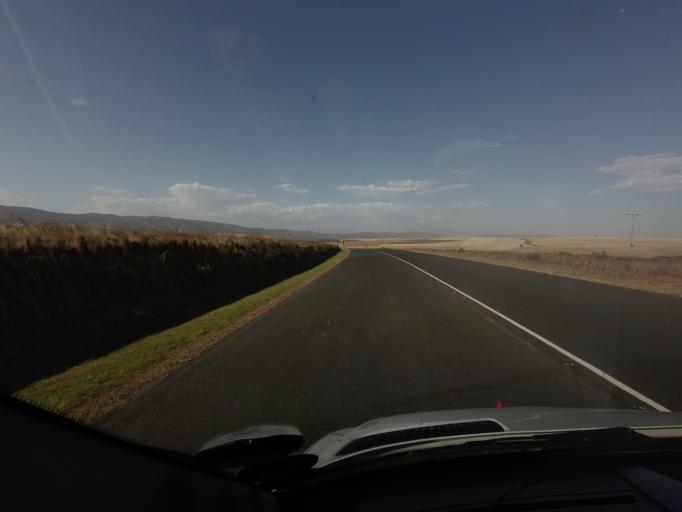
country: ZA
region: Western Cape
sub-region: Cape Winelands District Municipality
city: Ashton
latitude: -34.1372
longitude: 20.0258
